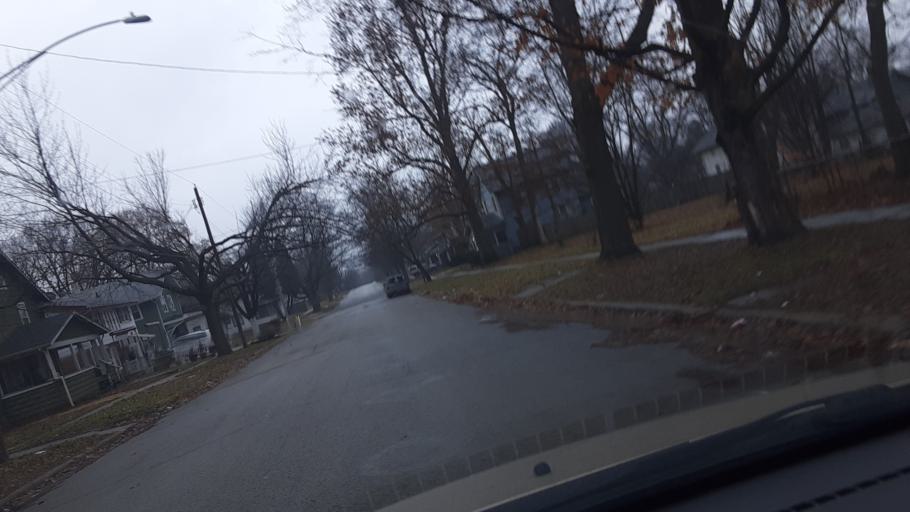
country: US
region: Illinois
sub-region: Winnebago County
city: Rockford
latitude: 42.2791
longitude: -89.1208
